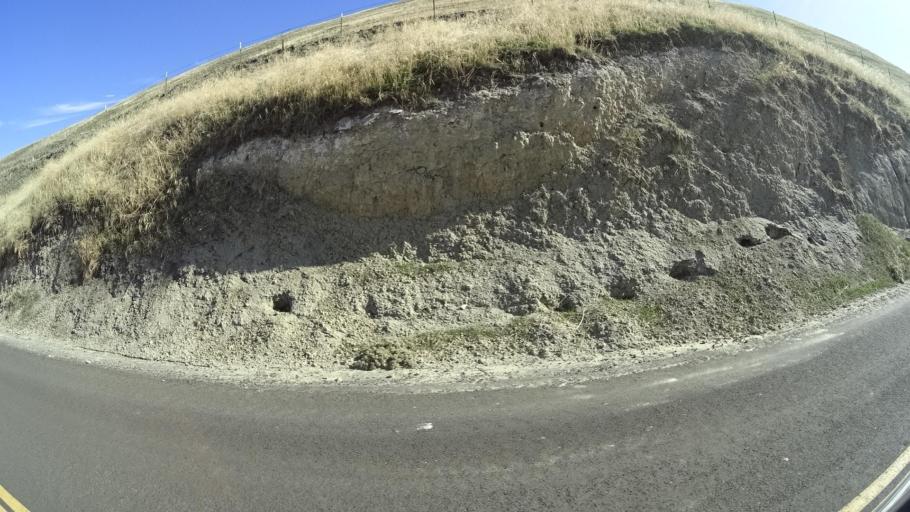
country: US
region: California
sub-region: Tulare County
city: Richgrove
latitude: 35.6683
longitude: -118.9147
